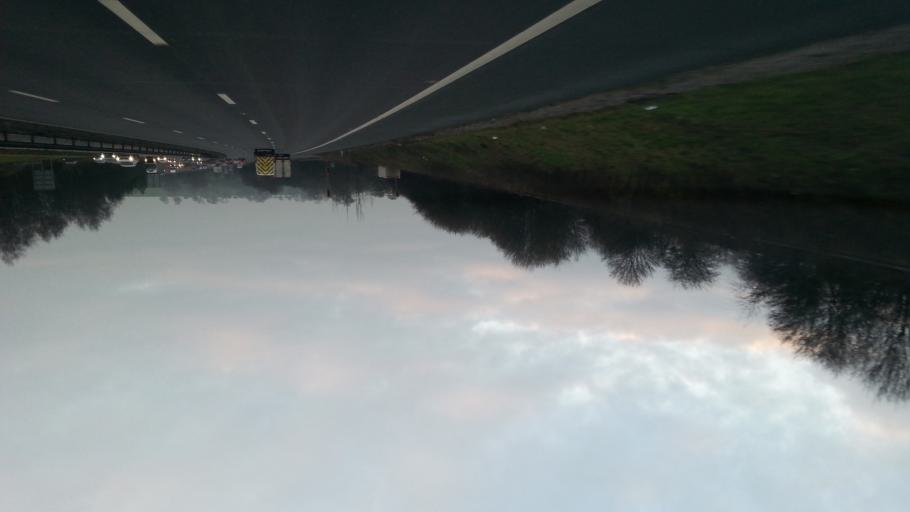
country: GB
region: England
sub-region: Worcestershire
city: Alvechurch
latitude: 52.3620
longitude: -1.9470
